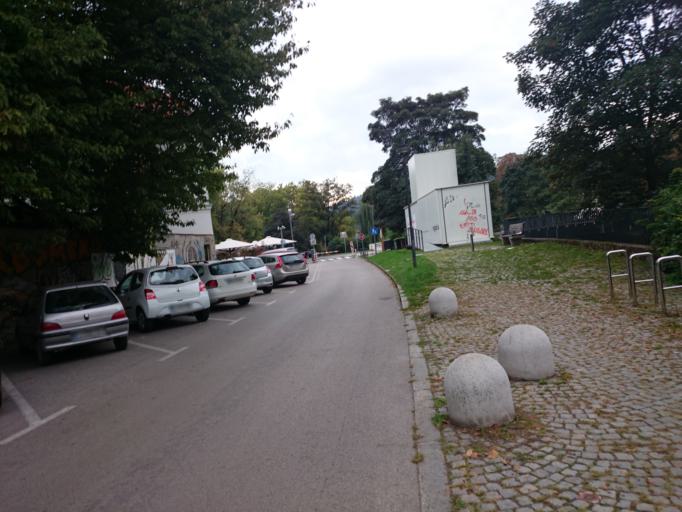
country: SI
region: Ljubljana
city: Ljubljana
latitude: 46.0509
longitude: 14.5158
